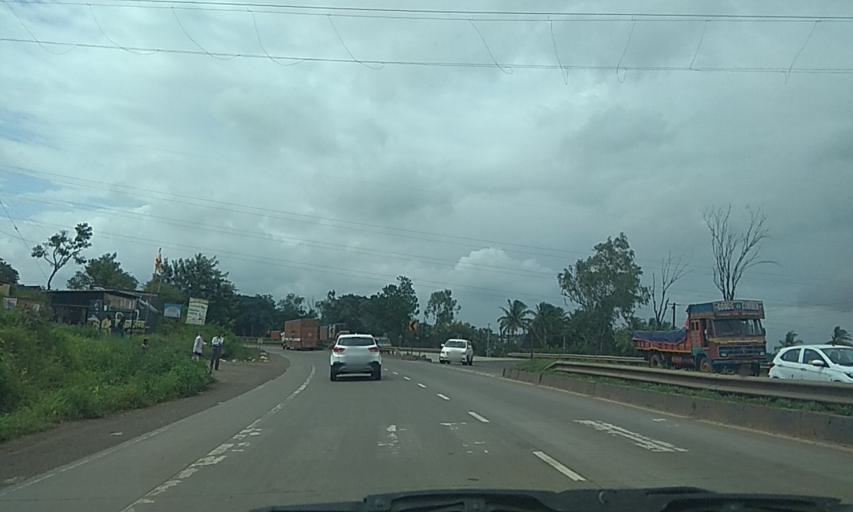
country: IN
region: Maharashtra
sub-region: Kolhapur
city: Kagal
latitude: 16.6308
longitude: 74.2915
